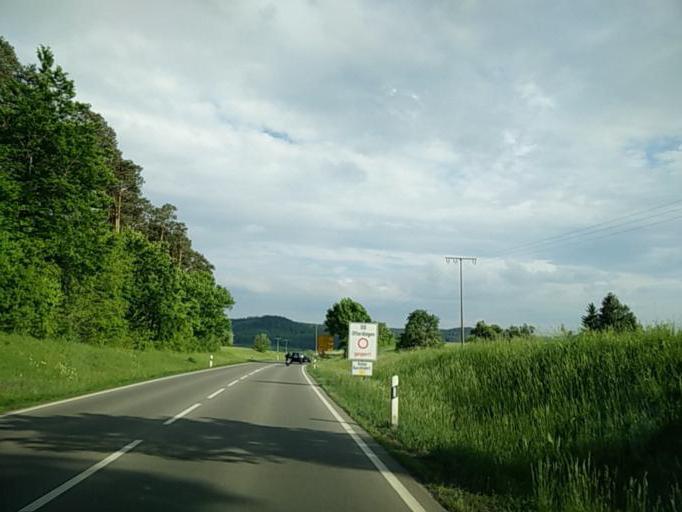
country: DE
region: Baden-Wuerttemberg
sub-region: Tuebingen Region
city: Rottenburg
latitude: 48.4431
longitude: 8.9220
